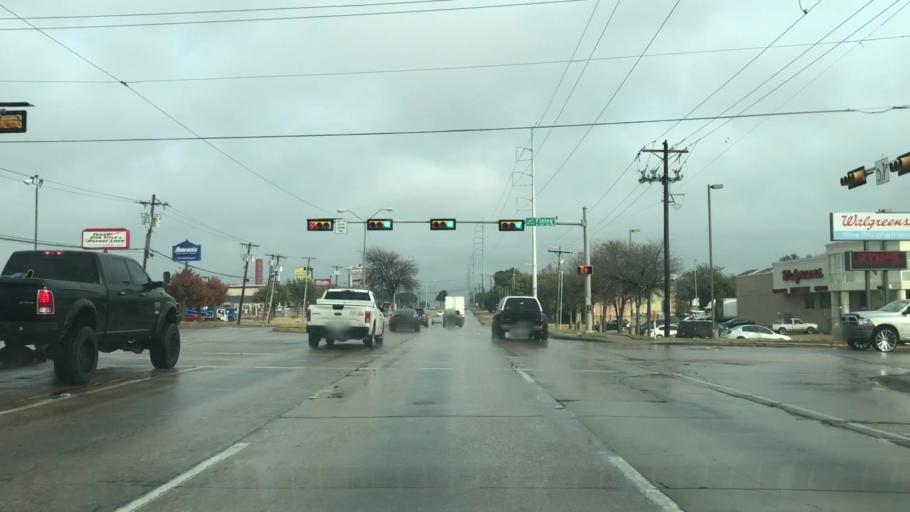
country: US
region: Texas
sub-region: Dallas County
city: Irving
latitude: 32.8507
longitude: -96.9921
